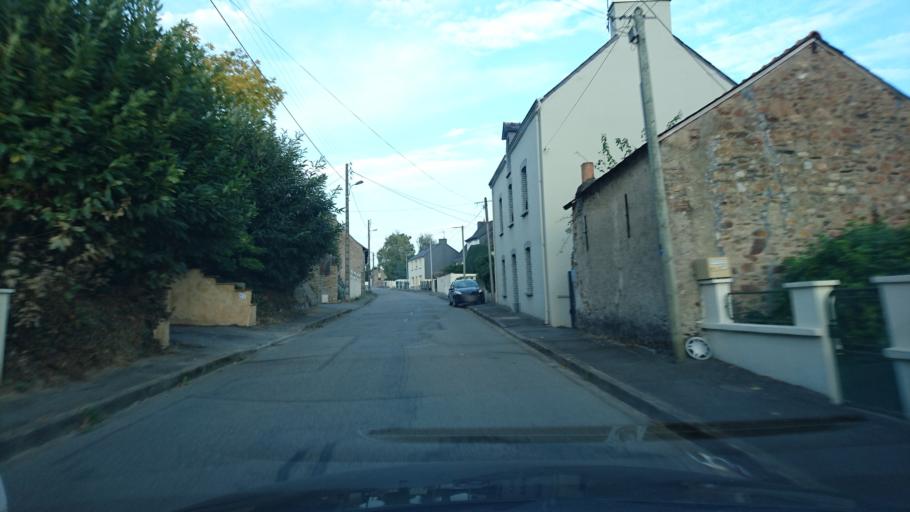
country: FR
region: Brittany
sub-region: Departement d'Ille-et-Vilaine
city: Redon
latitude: 47.6605
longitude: -2.0881
